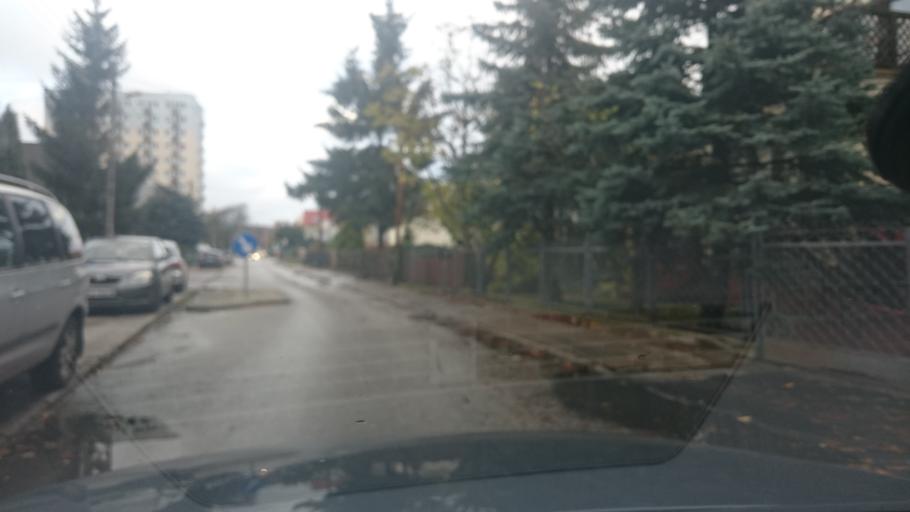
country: PL
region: Pomeranian Voivodeship
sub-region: Sopot
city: Sopot
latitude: 54.4011
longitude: 18.5802
